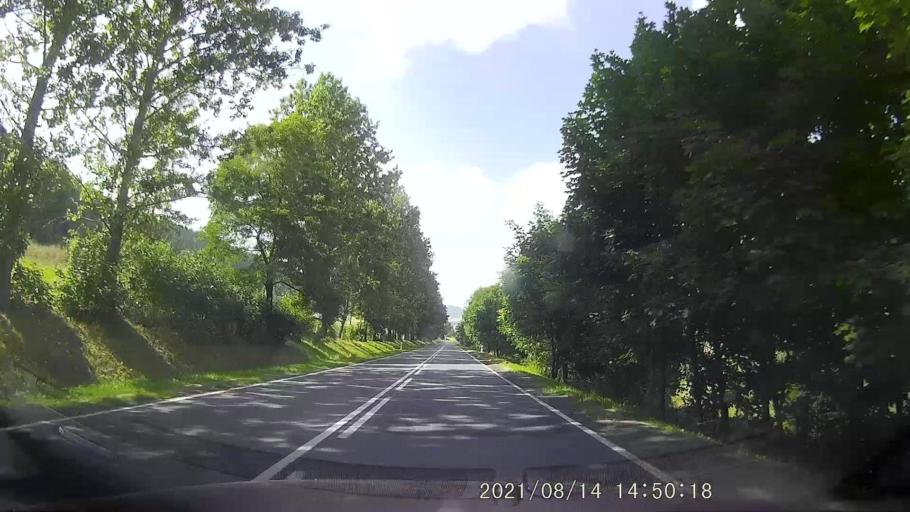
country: PL
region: Lower Silesian Voivodeship
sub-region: Powiat walbrzyski
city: Gluszyca Gorna
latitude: 50.6505
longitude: 16.3820
